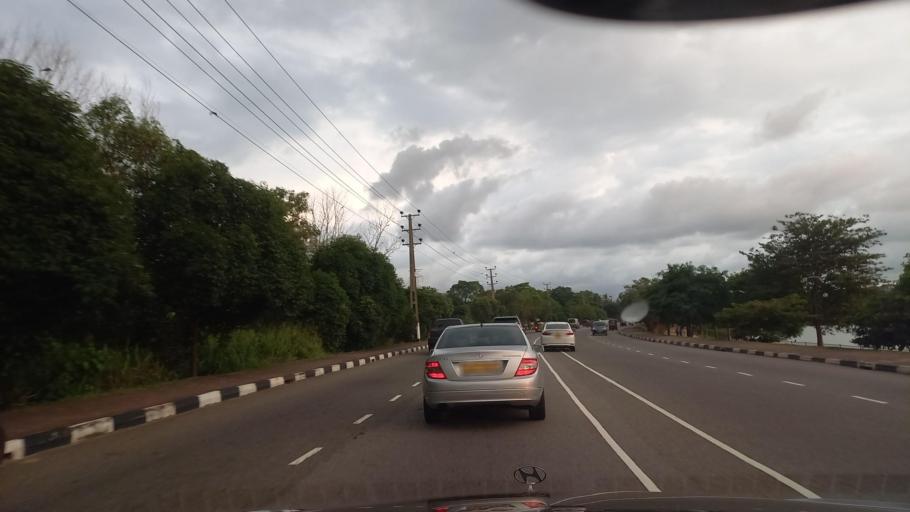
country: LK
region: Western
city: Battaramulla South
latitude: 6.8811
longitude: 79.9281
